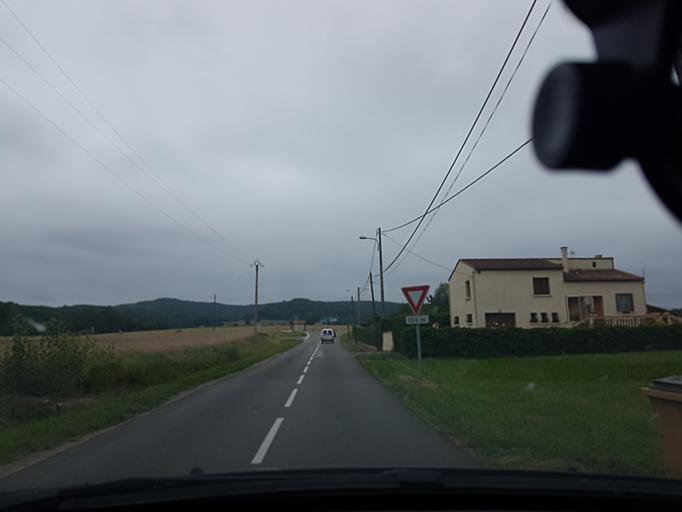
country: FR
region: Midi-Pyrenees
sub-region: Departement de l'Ariege
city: Mirepoix
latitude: 43.0779
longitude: 1.7736
